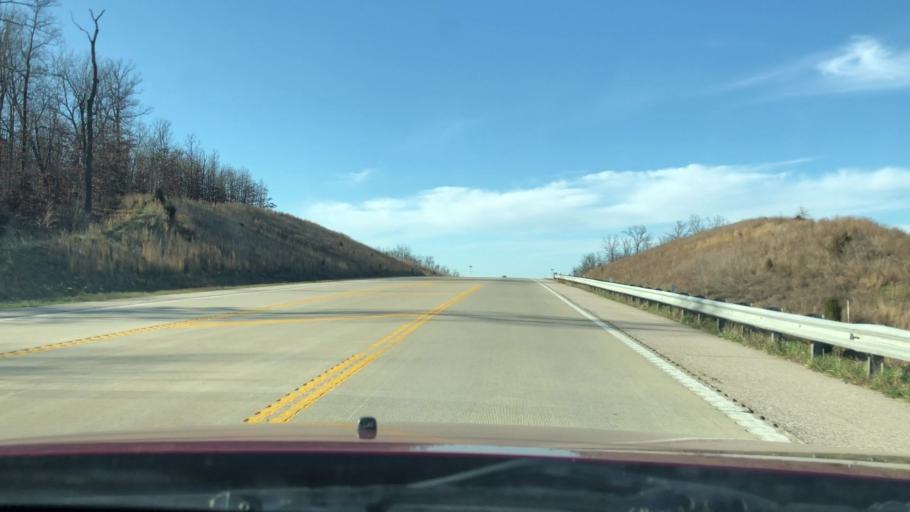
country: US
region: Missouri
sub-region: Camden County
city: Camdenton
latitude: 37.9336
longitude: -92.7146
